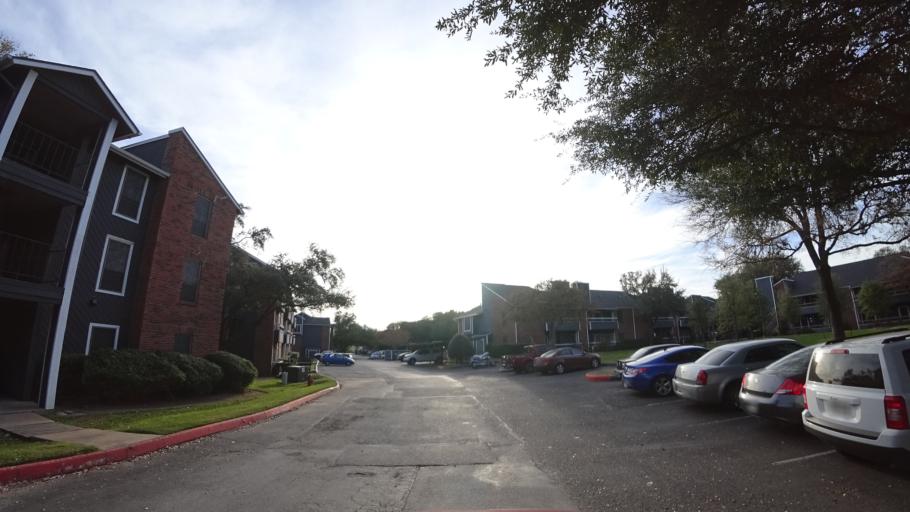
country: US
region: Texas
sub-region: Williamson County
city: Jollyville
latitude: 30.3930
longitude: -97.7545
